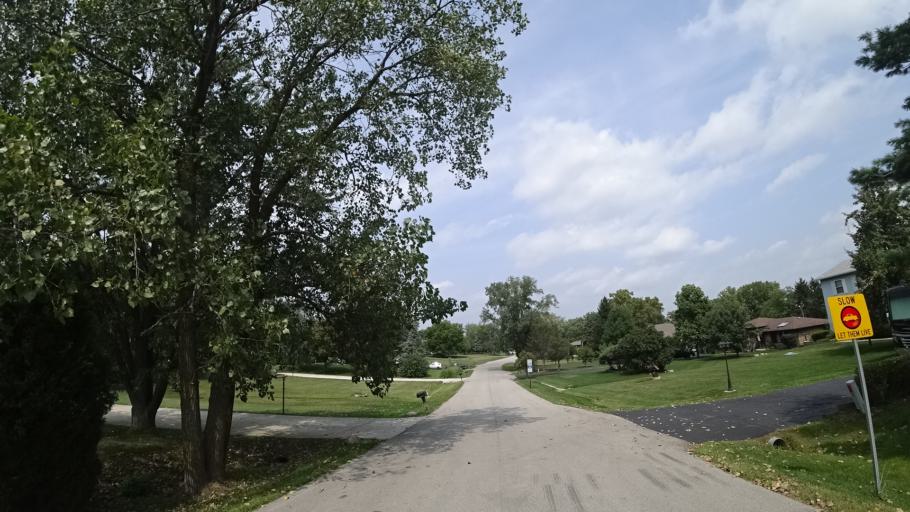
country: US
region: Illinois
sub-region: Will County
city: Goodings Grove
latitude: 41.6152
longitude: -87.9149
